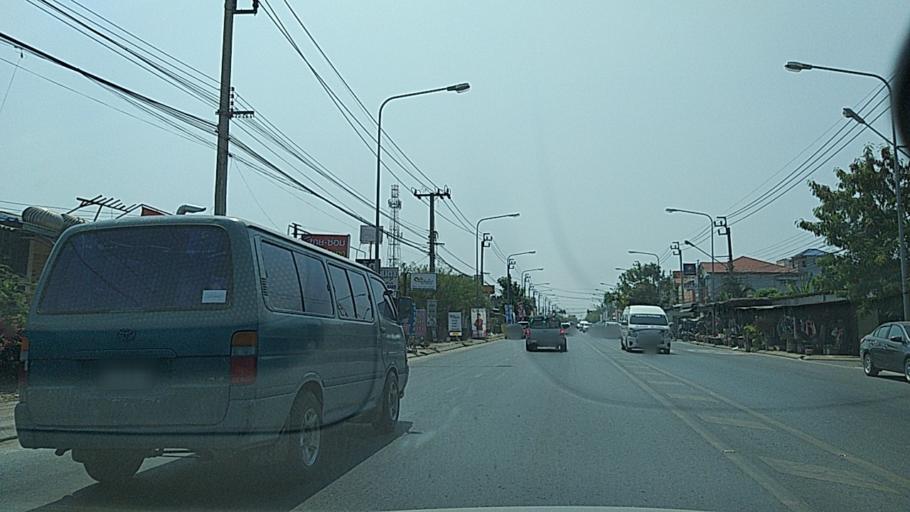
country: TH
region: Nonthaburi
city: Bang Yai
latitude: 13.9094
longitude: 100.3556
